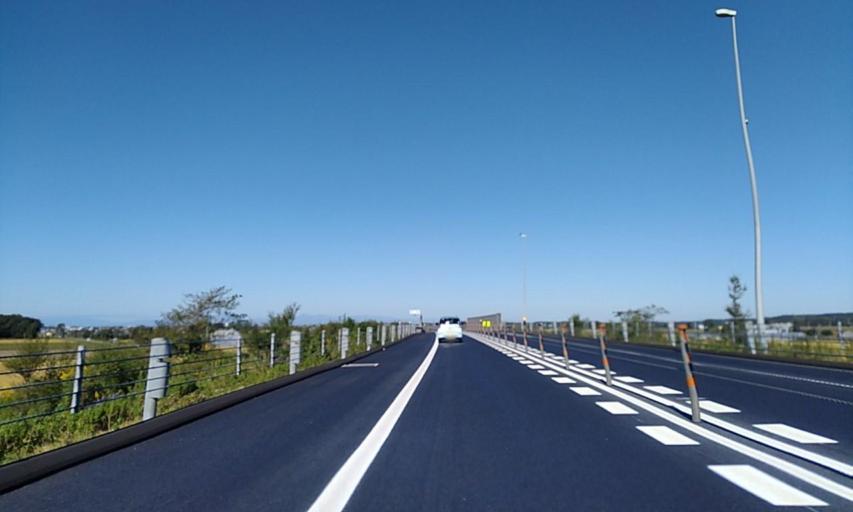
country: JP
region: Hokkaido
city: Tomakomai
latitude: 42.5747
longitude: 141.9696
